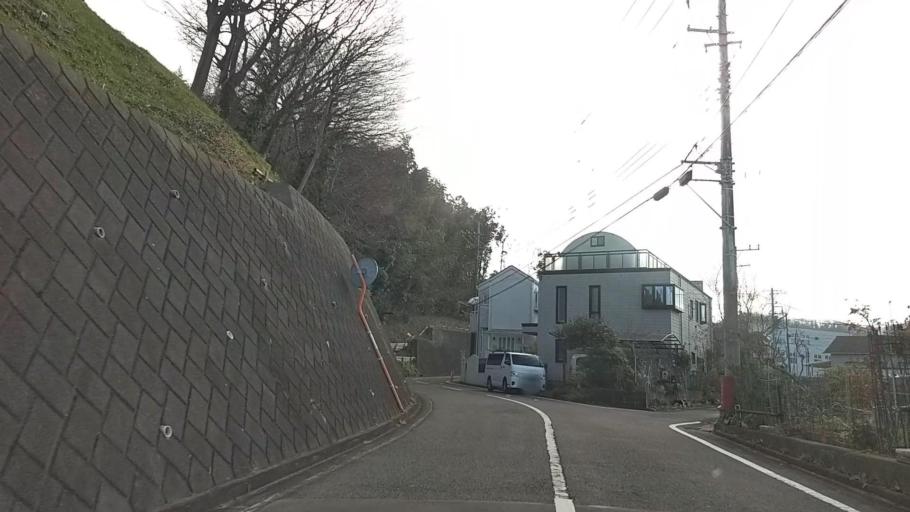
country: JP
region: Kanagawa
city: Atsugi
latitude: 35.4317
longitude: 139.3194
